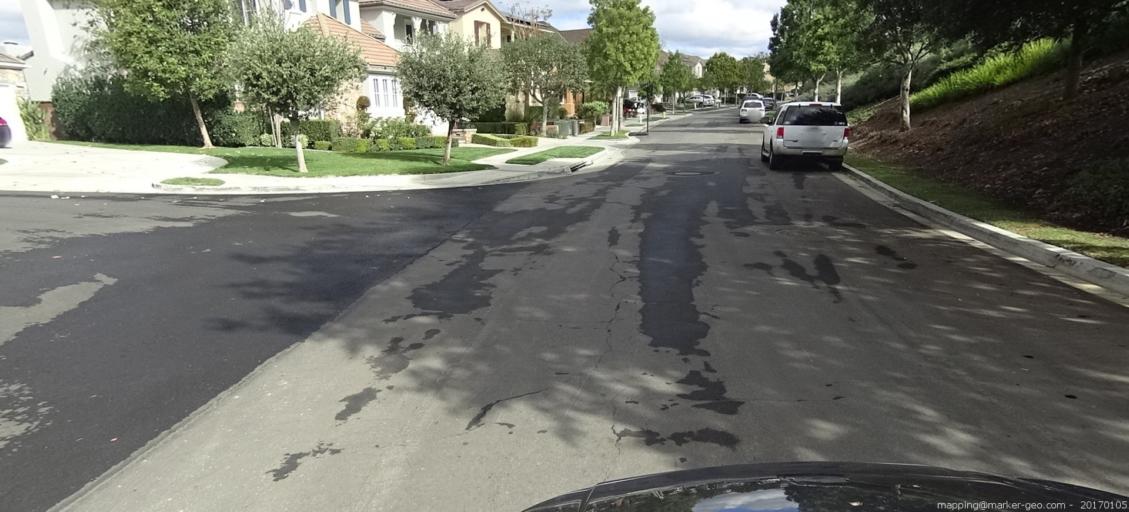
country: US
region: California
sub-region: Orange County
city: Ladera Ranch
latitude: 33.5644
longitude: -117.6421
